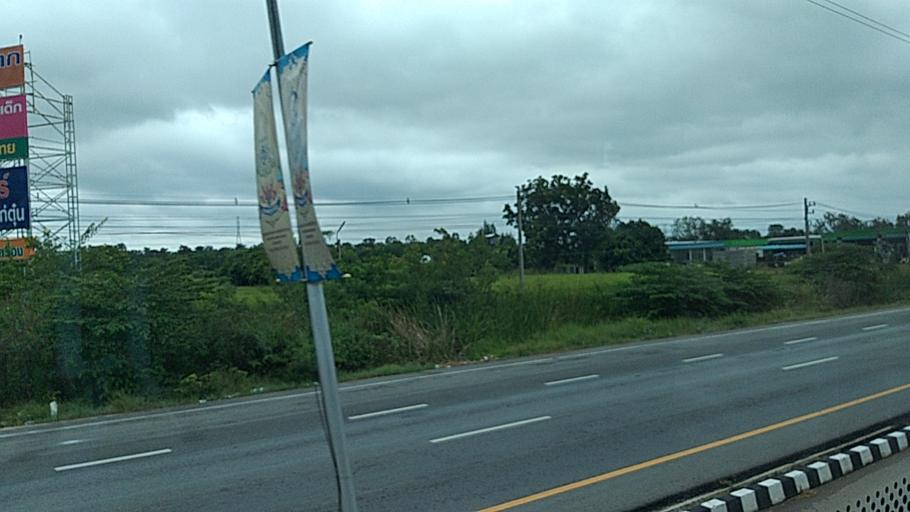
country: TH
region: Khon Kaen
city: Phon
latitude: 15.7222
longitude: 102.5923
